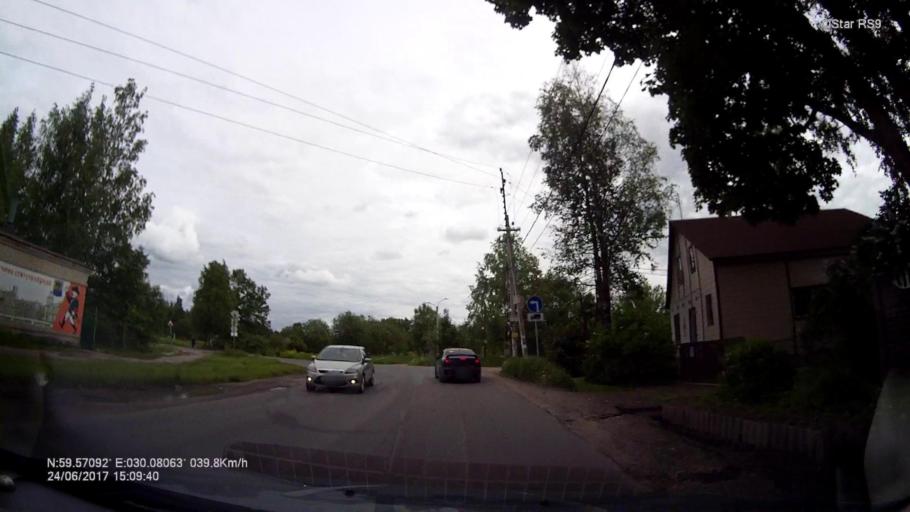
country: RU
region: Leningrad
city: Mariyenburg
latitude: 59.5708
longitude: 30.0807
